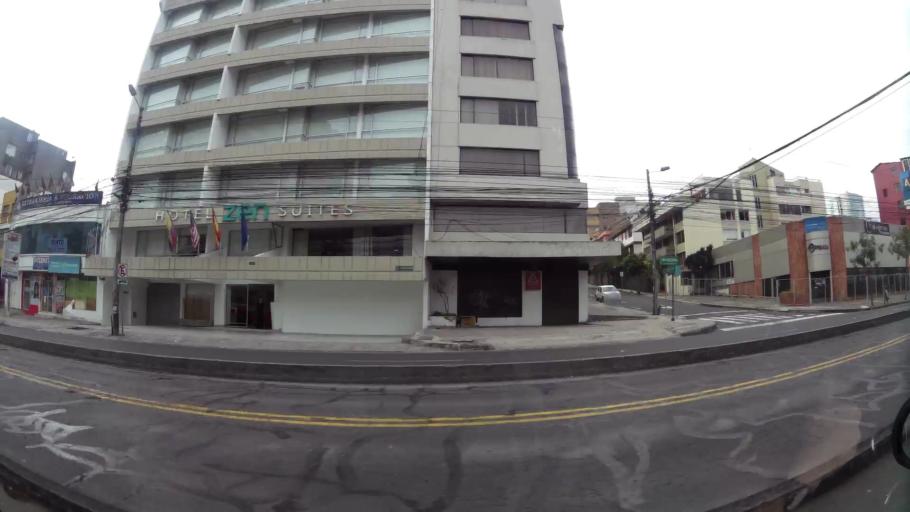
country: EC
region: Pichincha
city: Quito
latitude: -0.2003
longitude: -78.4851
